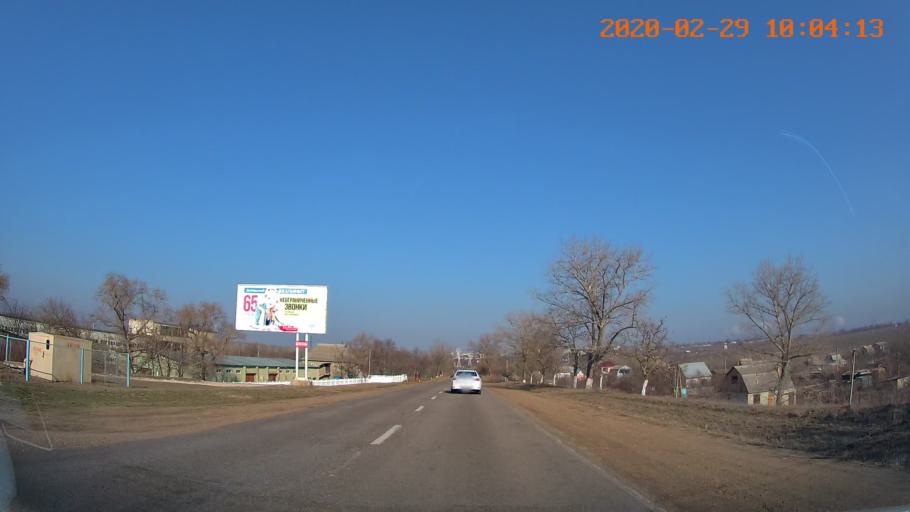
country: MD
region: Causeni
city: Chitcani
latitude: 46.7964
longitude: 29.6766
